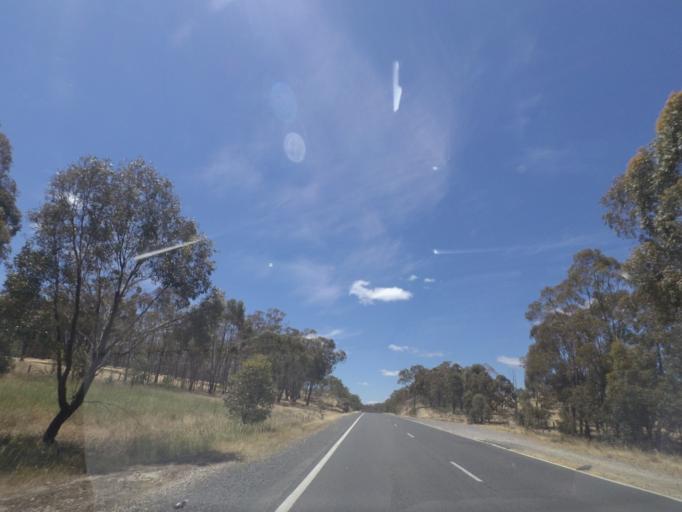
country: AU
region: Victoria
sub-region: Mount Alexander
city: Castlemaine
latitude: -37.1642
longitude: 144.1520
